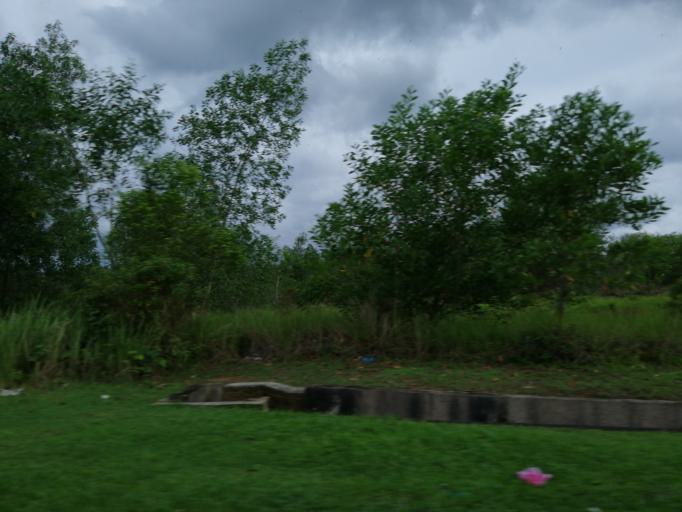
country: MY
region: Penang
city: Tasek Glugor
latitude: 5.4962
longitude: 100.6245
